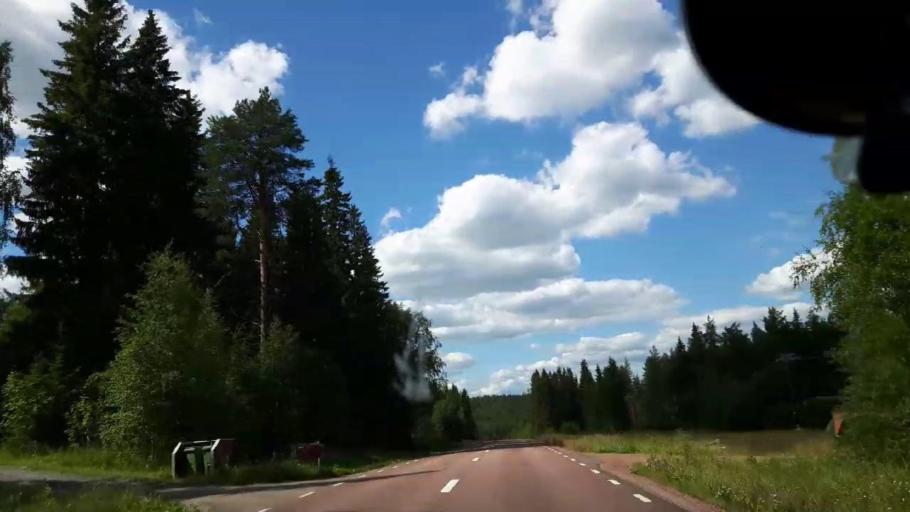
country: SE
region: Jaemtland
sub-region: Ragunda Kommun
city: Hammarstrand
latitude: 63.0198
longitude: 16.5549
